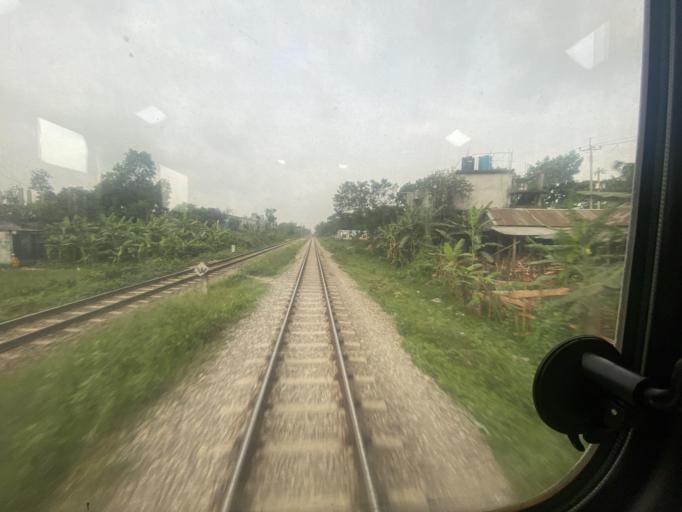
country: BD
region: Dhaka
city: Tungi
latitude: 23.9343
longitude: 90.4684
